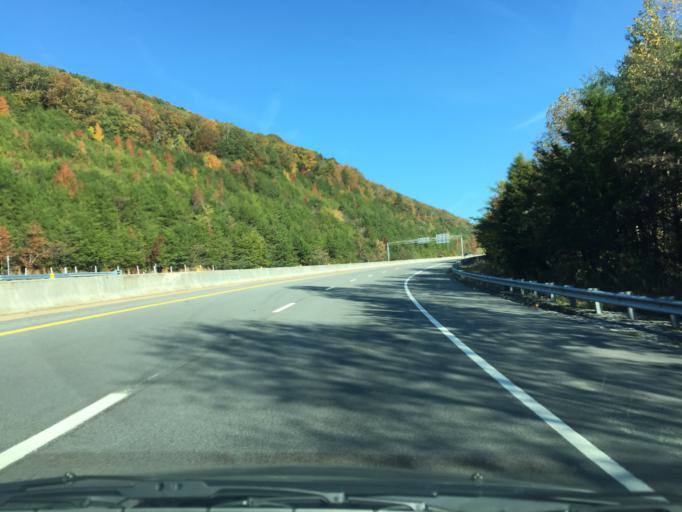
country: US
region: Tennessee
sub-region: Hamilton County
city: Soddy-Daisy
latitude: 35.3068
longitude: -85.1643
